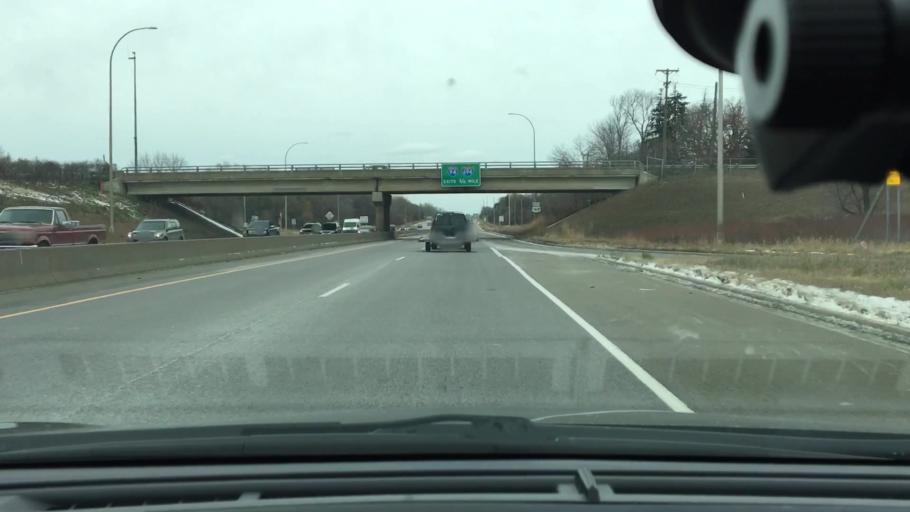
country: US
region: Minnesota
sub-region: Hennepin County
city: New Hope
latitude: 45.0686
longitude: -93.4009
